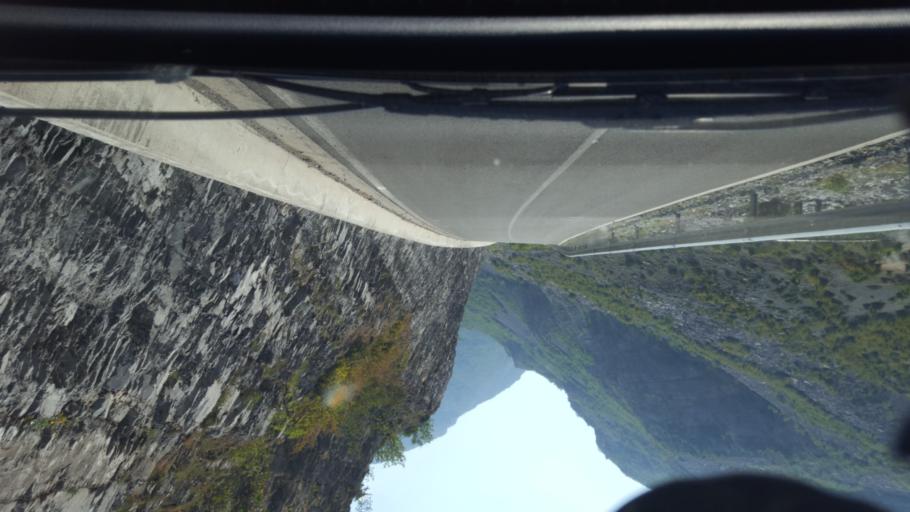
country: AL
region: Shkoder
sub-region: Rrethi i Malesia e Madhe
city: Kastrat
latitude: 42.5021
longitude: 19.5937
